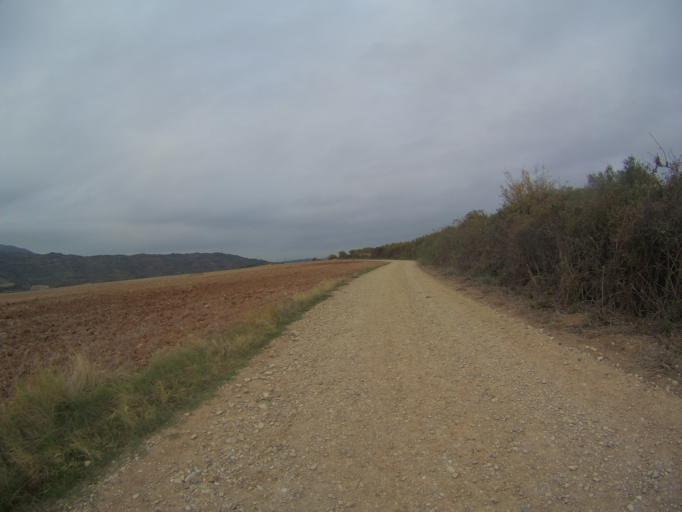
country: ES
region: Navarre
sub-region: Provincia de Navarra
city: Cirauqui
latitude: 42.6792
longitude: -1.9096
